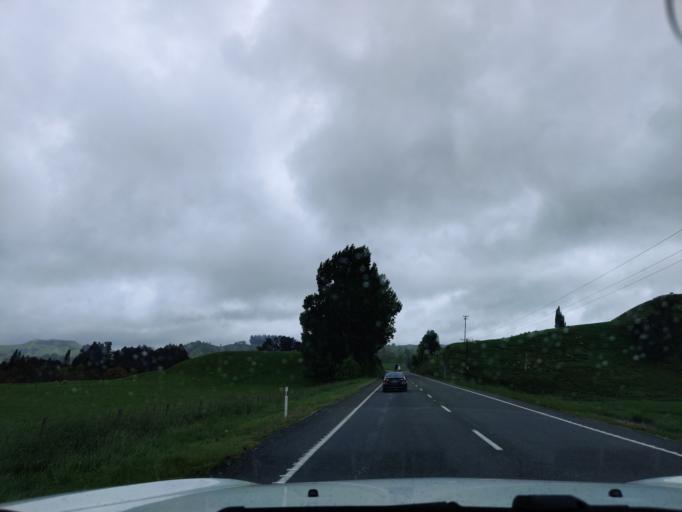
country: NZ
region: Manawatu-Wanganui
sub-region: Ruapehu District
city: Waiouru
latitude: -39.6391
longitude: 175.7683
